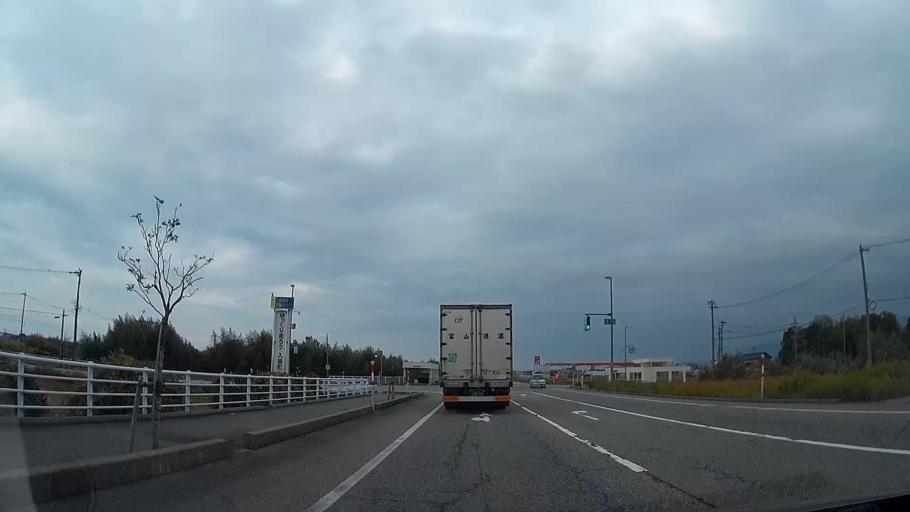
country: JP
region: Toyama
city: Nyuzen
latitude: 36.9121
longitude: 137.4574
